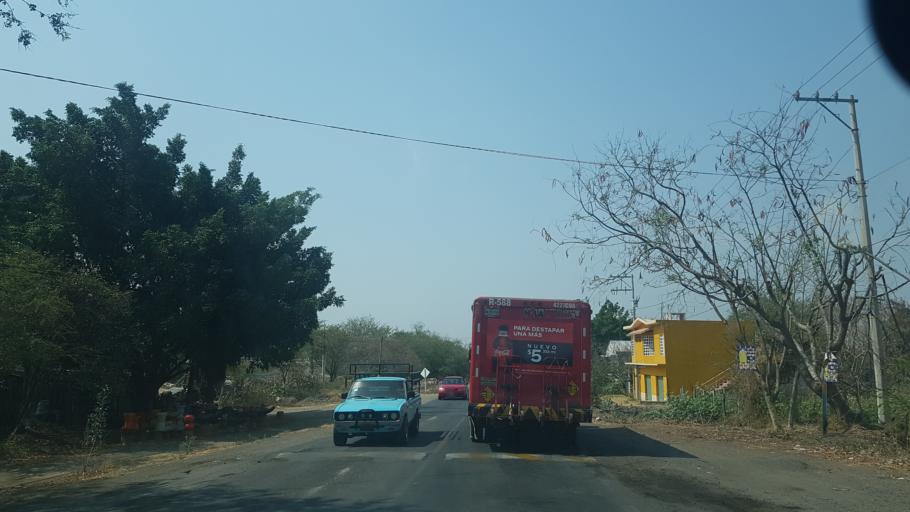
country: MX
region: Morelos
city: Amayuca
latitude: 18.7258
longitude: -98.7910
